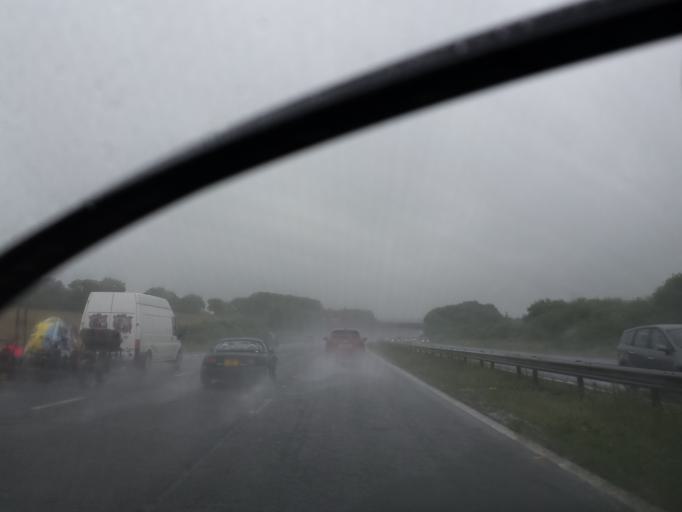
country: GB
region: England
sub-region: Leicestershire
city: Markfield
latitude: 52.6906
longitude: -1.2904
